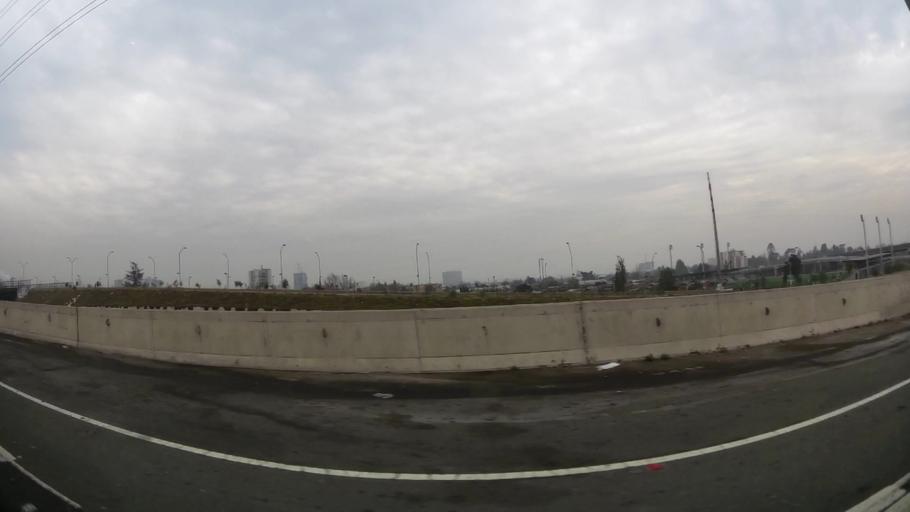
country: CL
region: Santiago Metropolitan
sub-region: Provincia de Santiago
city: Lo Prado
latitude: -33.4198
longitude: -70.6874
